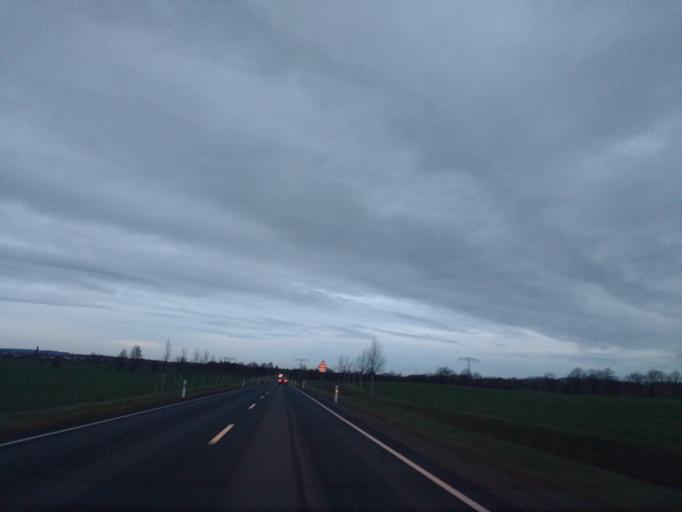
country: DE
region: Saxony-Anhalt
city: Quedlinburg
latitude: 51.7659
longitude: 11.1567
